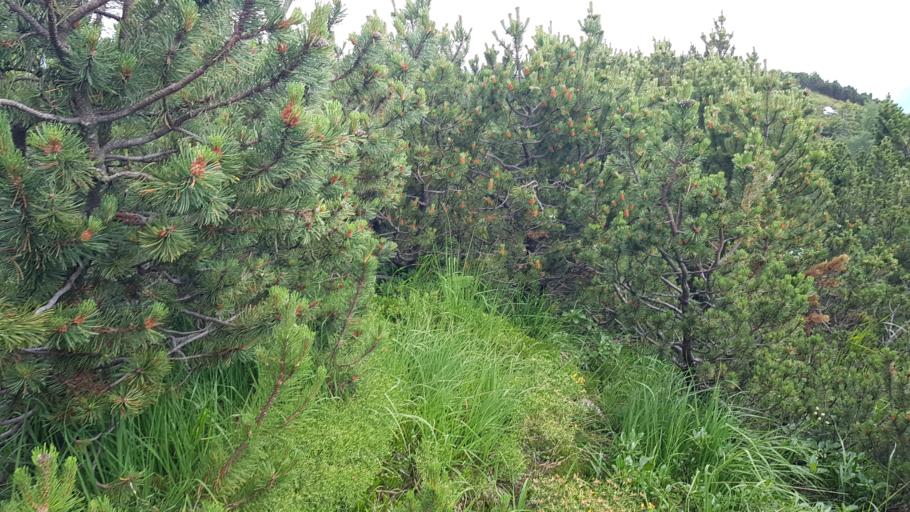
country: SI
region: Bovec
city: Bovec
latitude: 46.4094
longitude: 13.5777
